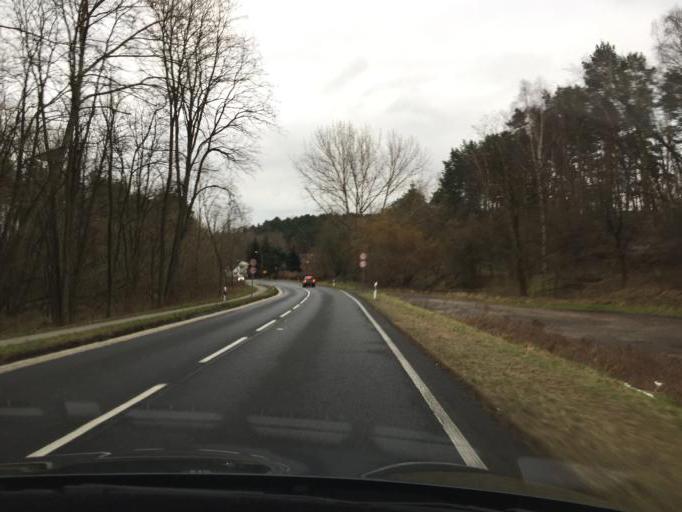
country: DE
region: Brandenburg
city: Eisenhuettenstadt
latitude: 52.1510
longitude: 14.5973
